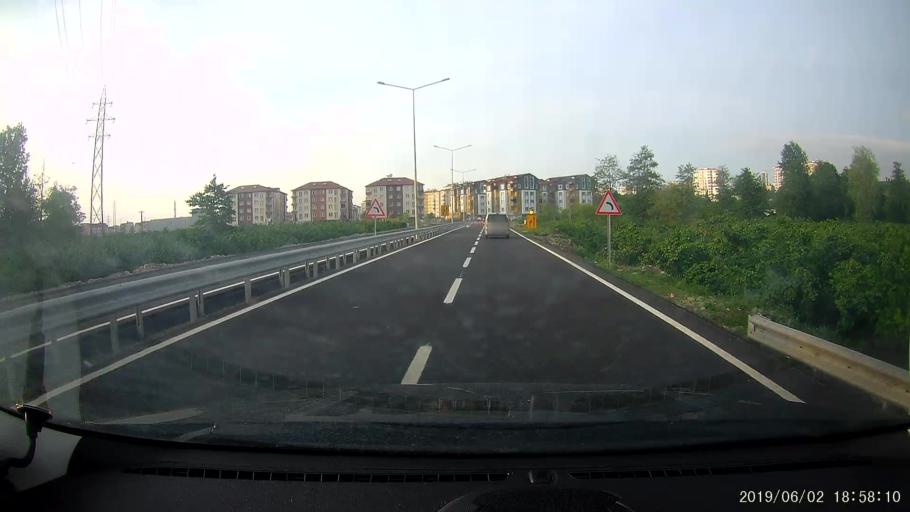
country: TR
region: Ordu
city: Ordu
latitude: 40.9593
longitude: 37.9073
